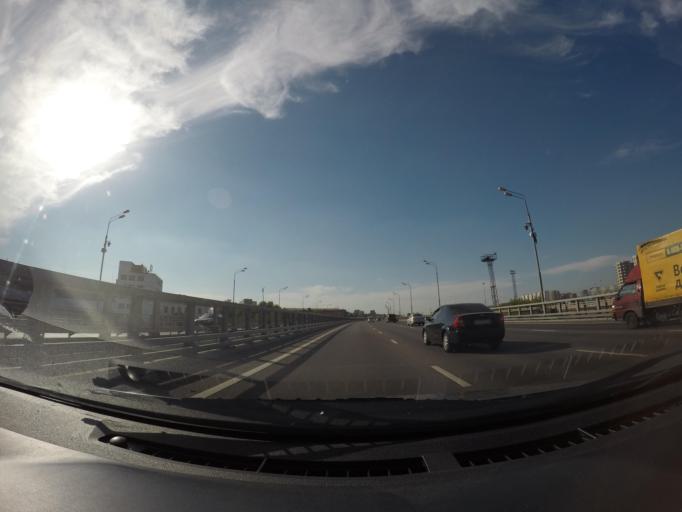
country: RU
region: Moscow
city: Zapadnoye Degunino
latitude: 55.8568
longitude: 37.5356
